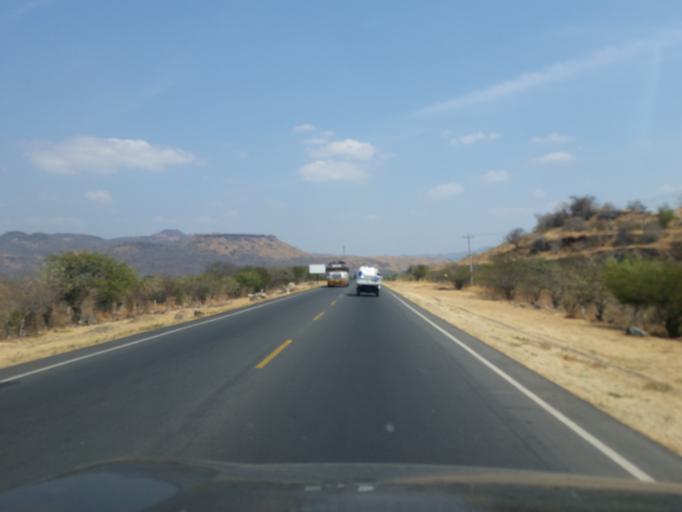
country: NI
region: Managua
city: Tipitapa
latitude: 12.4243
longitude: -86.0416
